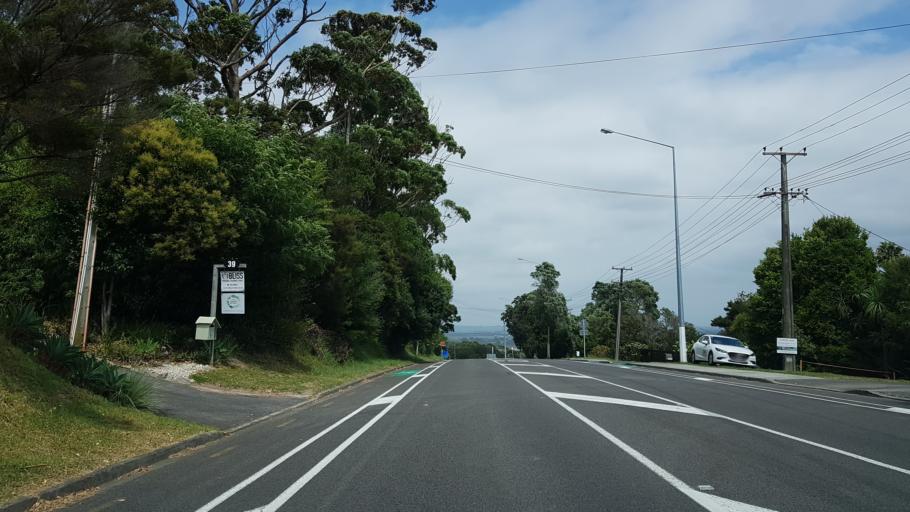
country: NZ
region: Auckland
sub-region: Auckland
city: North Shore
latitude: -36.7803
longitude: 174.6811
